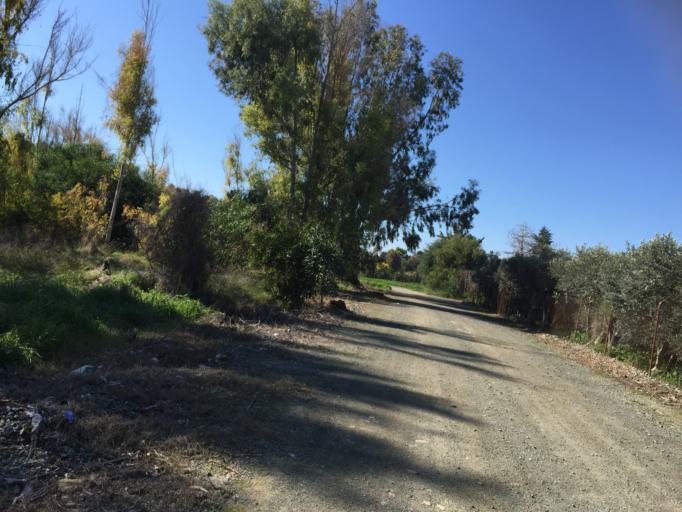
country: CY
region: Larnaka
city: Kolossi
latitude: 34.6318
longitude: 32.9624
